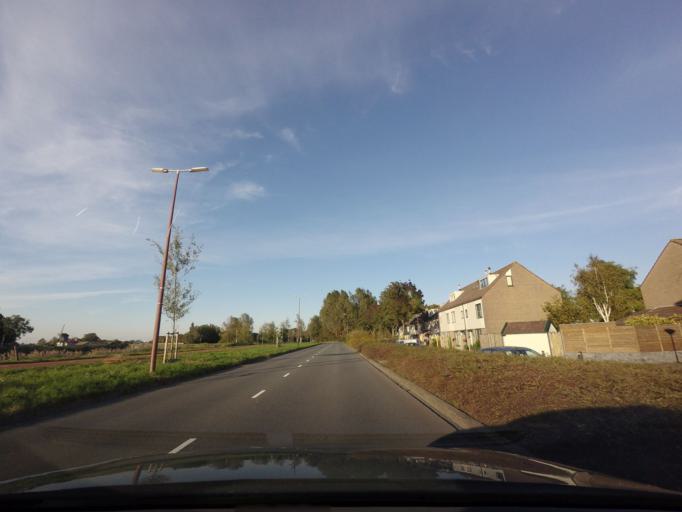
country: NL
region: North Holland
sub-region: Gemeente Alkmaar
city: Alkmaar
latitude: 52.6566
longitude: 4.7464
